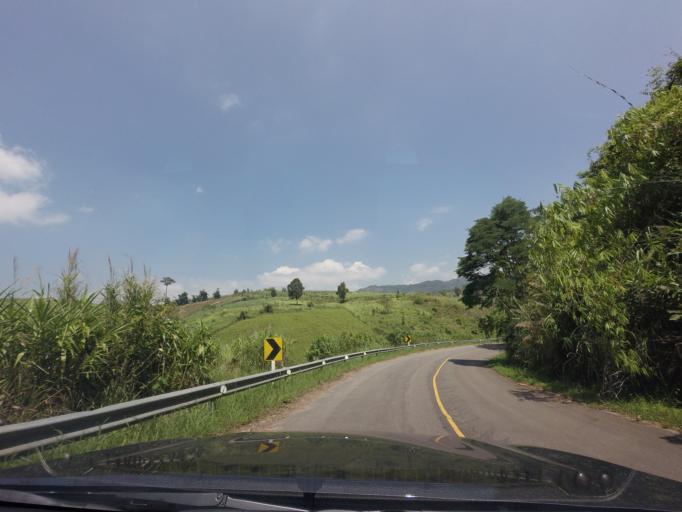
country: TH
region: Loei
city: Na Haeo
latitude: 17.5856
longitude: 100.9059
